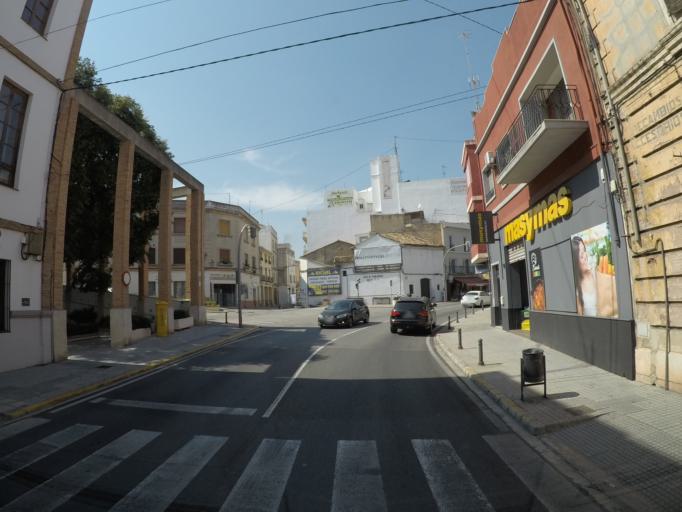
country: ES
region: Valencia
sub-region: Provincia de Valencia
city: Oliva
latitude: 38.9216
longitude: -0.1222
